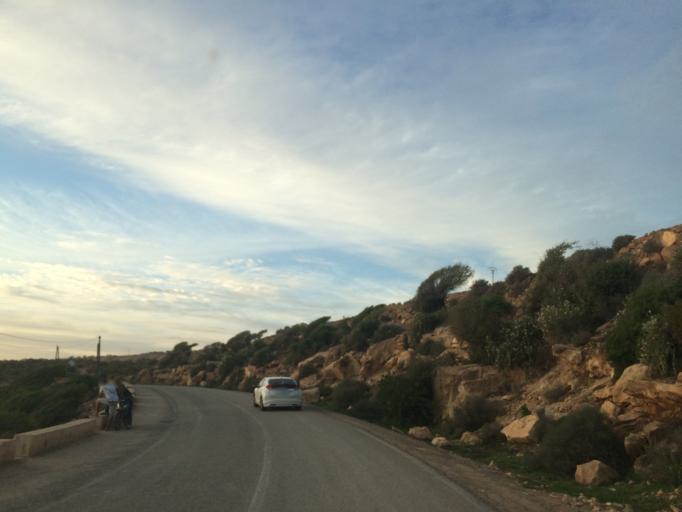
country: MA
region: Souss-Massa-Draa
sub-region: Agadir-Ida-ou-Tnan
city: Taghazout
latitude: 30.5466
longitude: -9.7151
